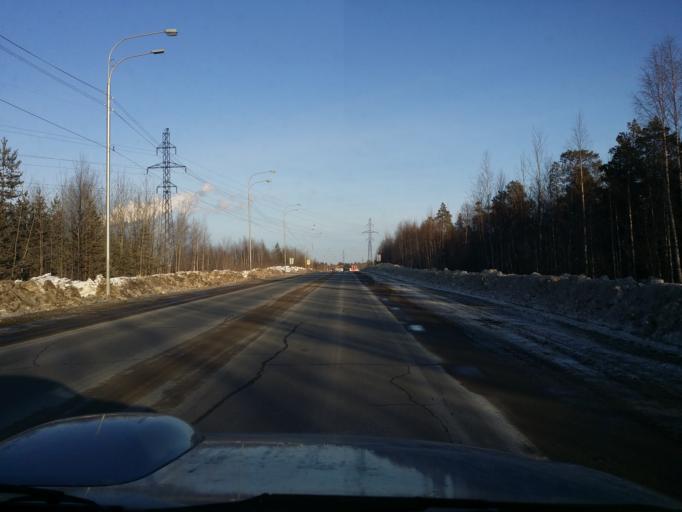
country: RU
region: Khanty-Mansiyskiy Avtonomnyy Okrug
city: Izluchinsk
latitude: 60.9644
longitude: 76.8657
